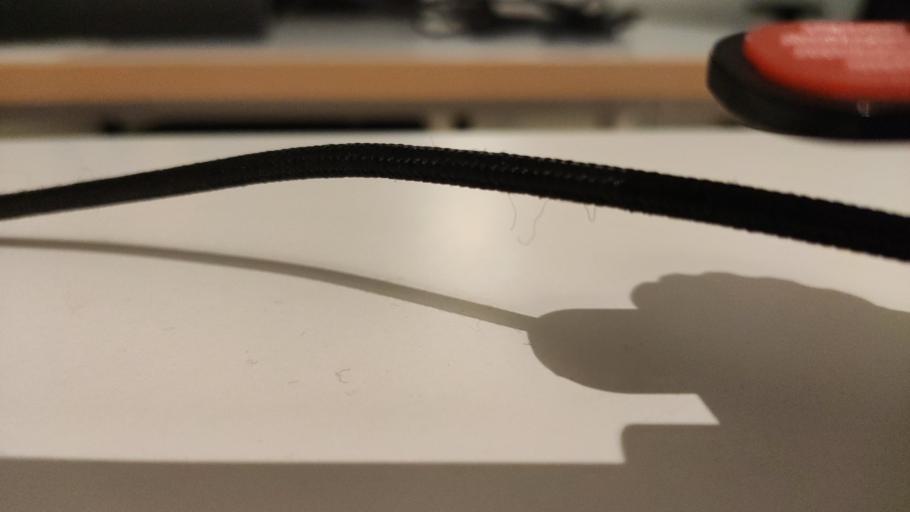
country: RU
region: Moskovskaya
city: Gorshkovo
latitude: 56.3696
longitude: 37.4386
